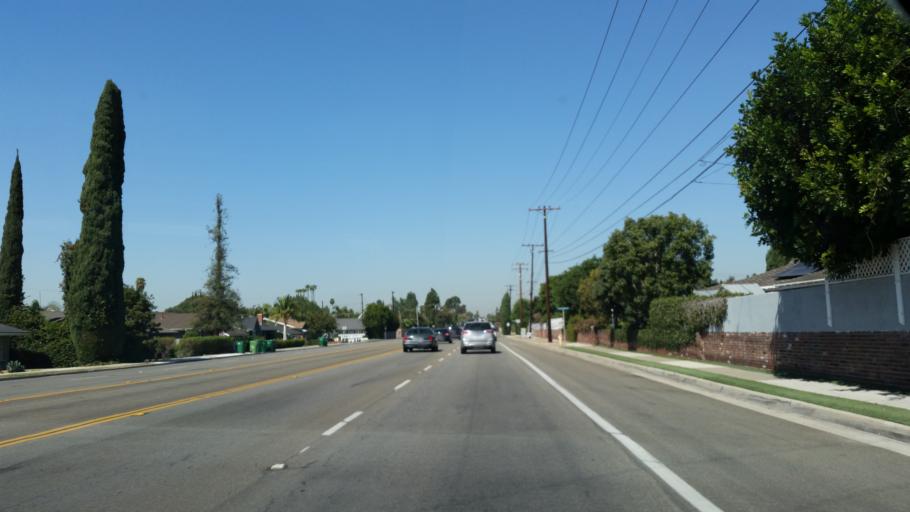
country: US
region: California
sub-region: Orange County
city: North Tustin
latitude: 33.7414
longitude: -117.7994
